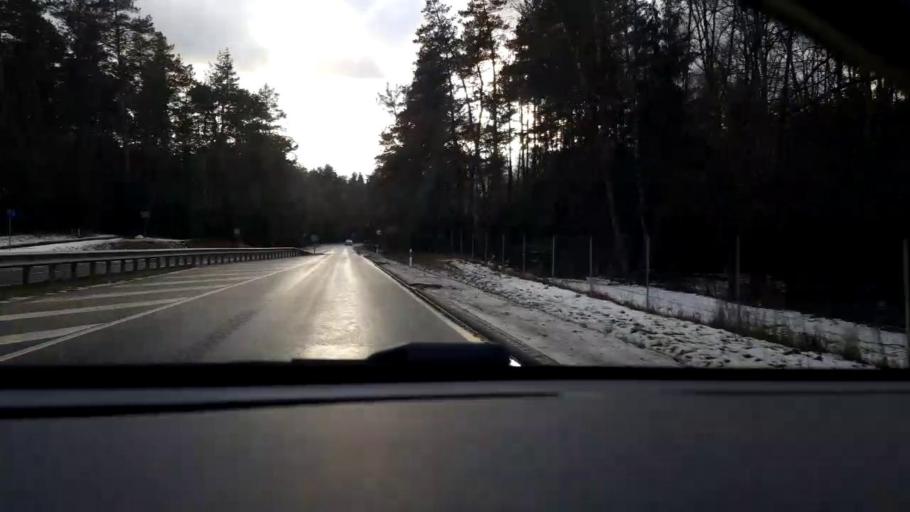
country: LT
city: Nemencine
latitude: 54.8046
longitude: 25.4091
